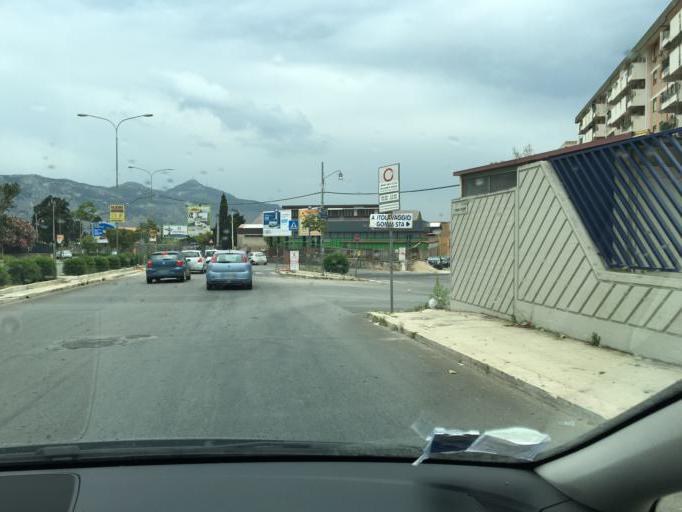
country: IT
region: Sicily
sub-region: Palermo
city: Isola delle Femmine
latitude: 38.1893
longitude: 13.2945
